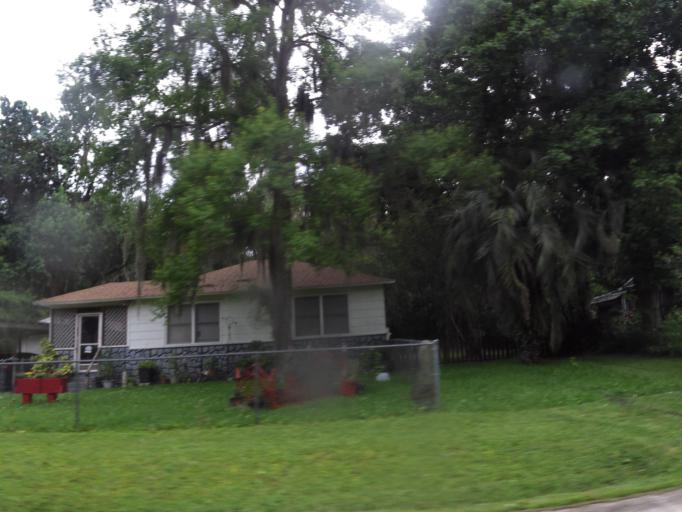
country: US
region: Florida
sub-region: Duval County
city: Jacksonville
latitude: 30.2914
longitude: -81.5443
